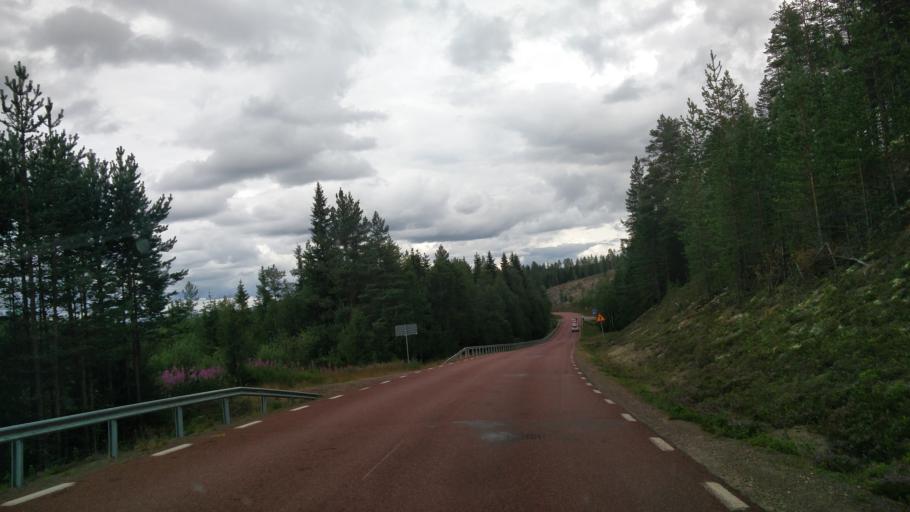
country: NO
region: Hedmark
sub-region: Trysil
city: Innbygda
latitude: 61.1493
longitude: 12.8010
